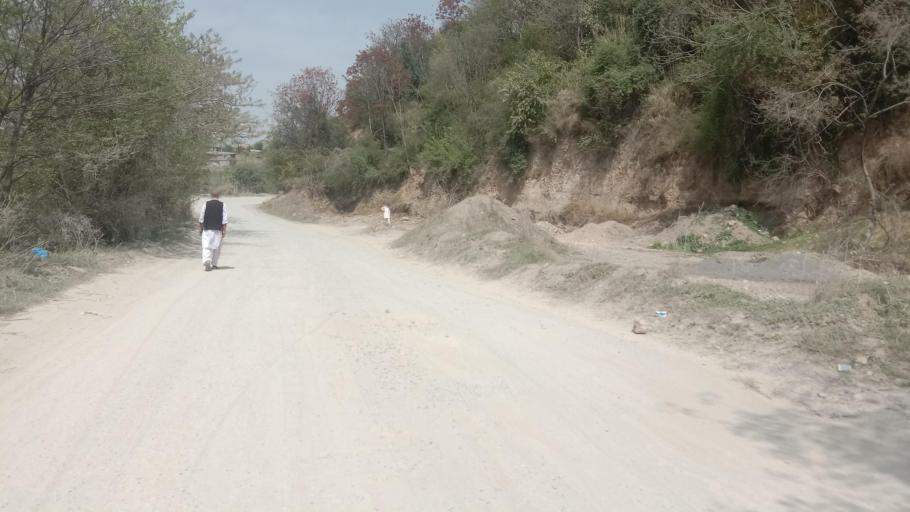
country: PK
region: Khyber Pakhtunkhwa
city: Abbottabad
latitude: 34.1574
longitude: 73.2681
